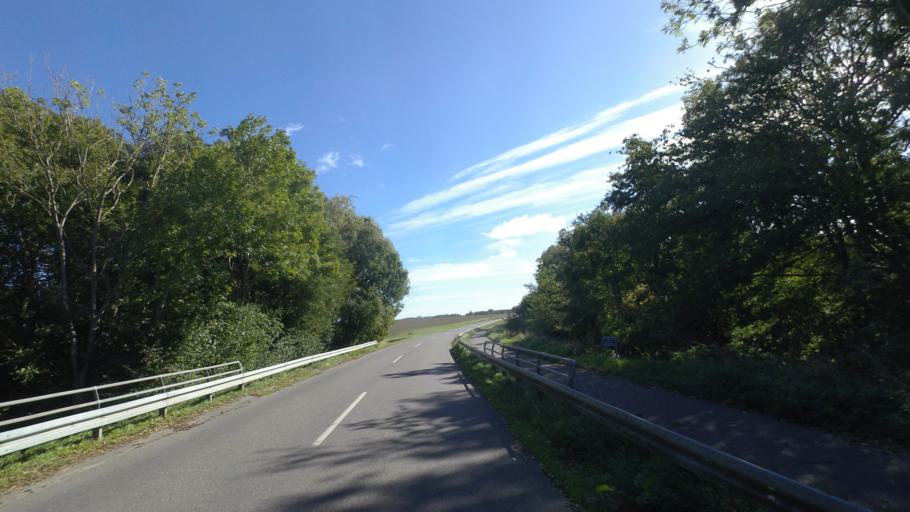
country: DK
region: Capital Region
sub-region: Bornholm Kommune
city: Akirkeby
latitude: 55.0084
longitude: 14.9955
